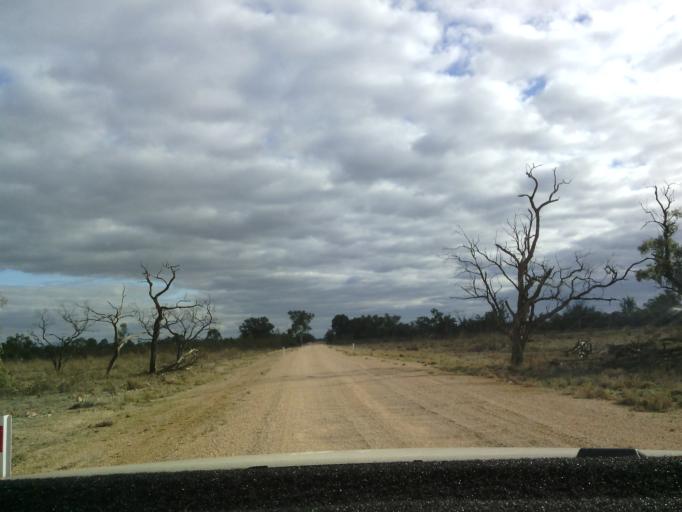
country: AU
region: South Australia
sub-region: Renmark Paringa
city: Renmark
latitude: -34.1662
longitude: 141.1891
